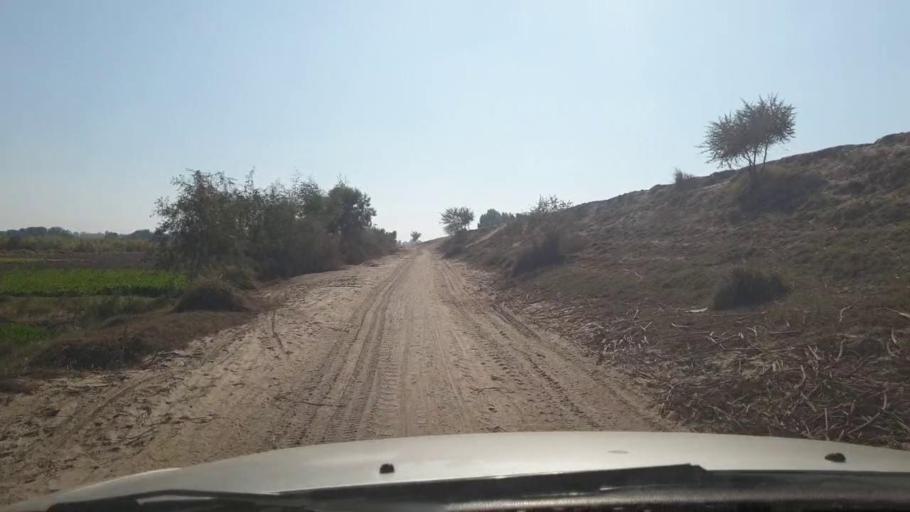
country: PK
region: Sindh
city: Ghotki
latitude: 28.0218
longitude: 69.2096
